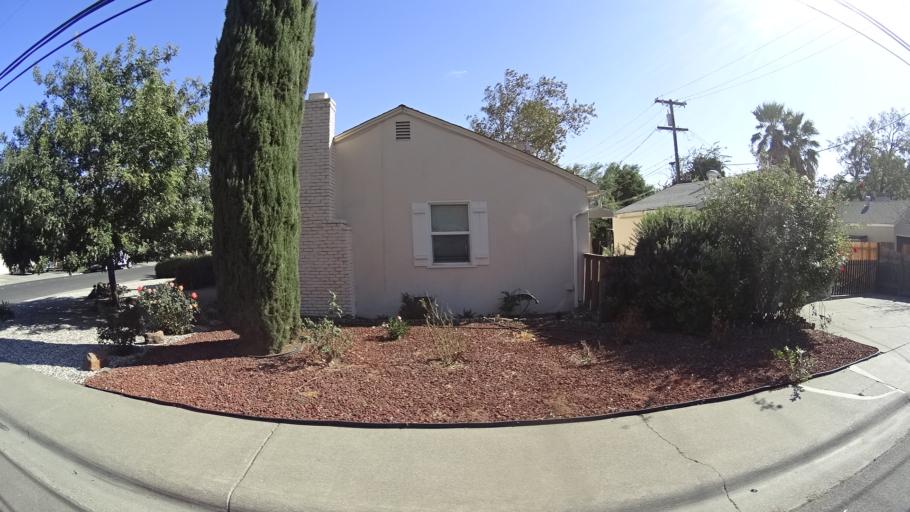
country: US
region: California
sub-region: Yolo County
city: Woodland
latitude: 38.6701
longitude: -121.7841
